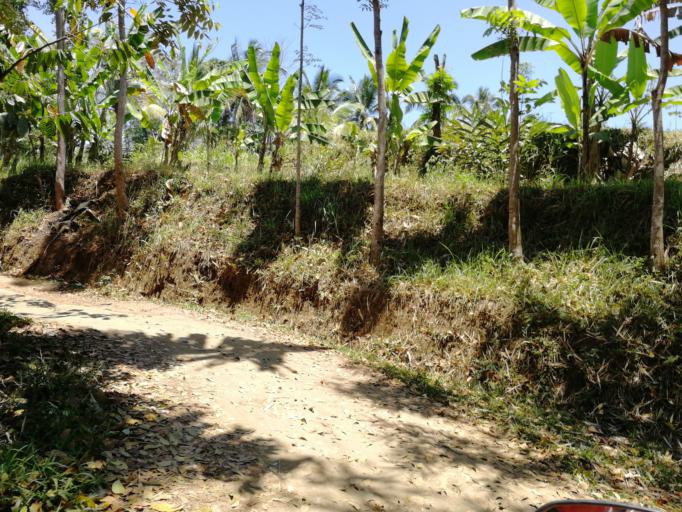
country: ID
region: West Nusa Tenggara
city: Tetebatu
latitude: -8.5478
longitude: 116.4198
